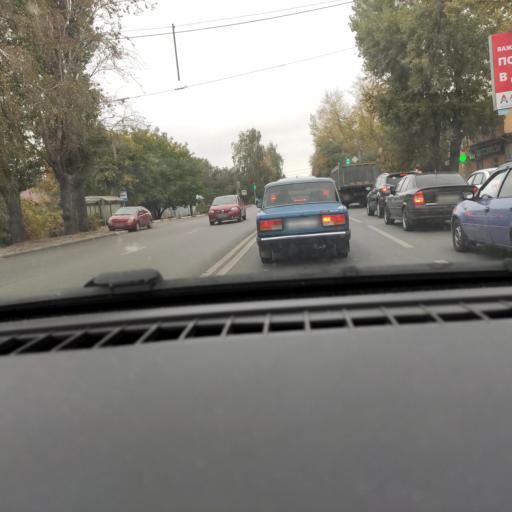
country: RU
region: Voronezj
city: Voronezh
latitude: 51.6930
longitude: 39.2039
